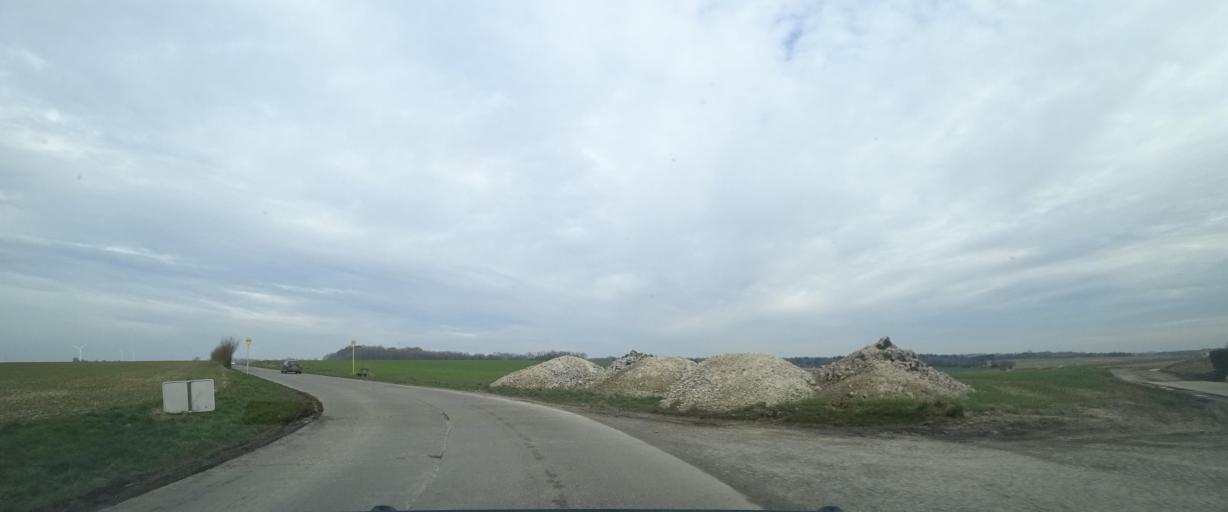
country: BE
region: Wallonia
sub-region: Province de Namur
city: Gembloux
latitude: 50.5240
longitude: 4.6596
